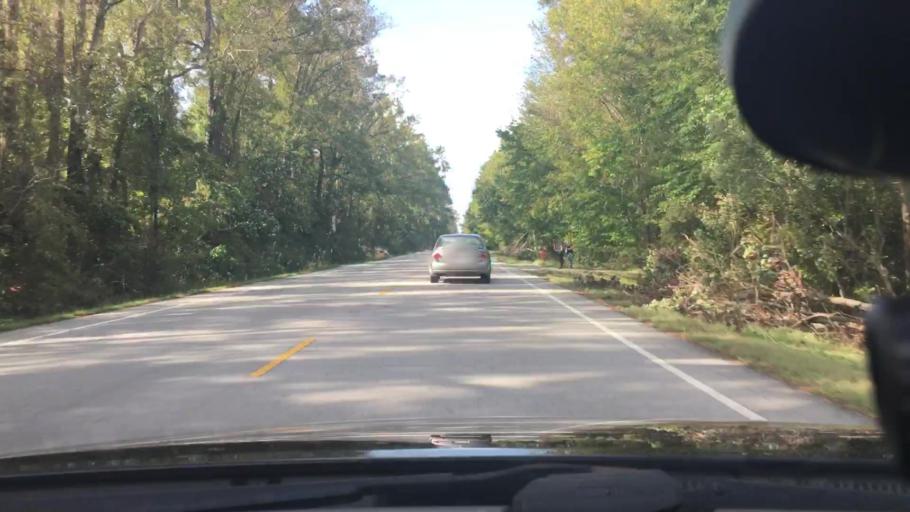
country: US
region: North Carolina
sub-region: Craven County
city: New Bern
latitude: 35.1826
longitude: -77.0485
